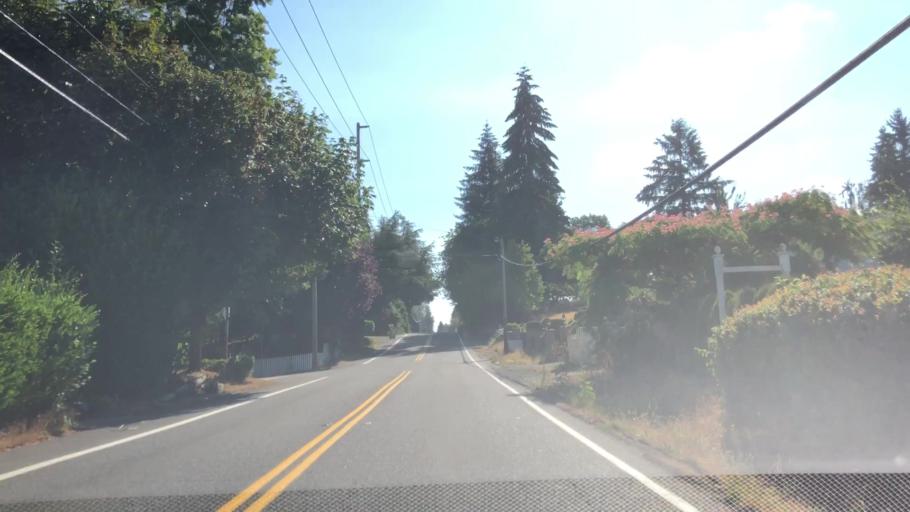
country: US
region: Washington
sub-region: King County
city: East Hill-Meridian
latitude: 47.4232
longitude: -122.2119
